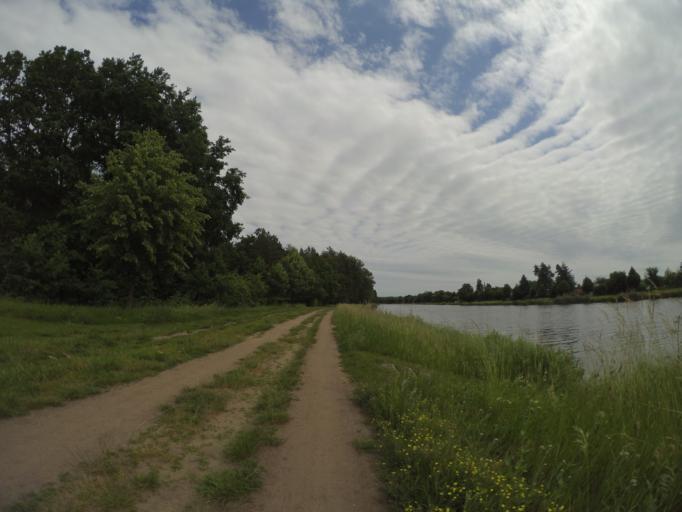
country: CZ
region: Central Bohemia
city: Celakovice
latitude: 50.1729
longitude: 14.7811
